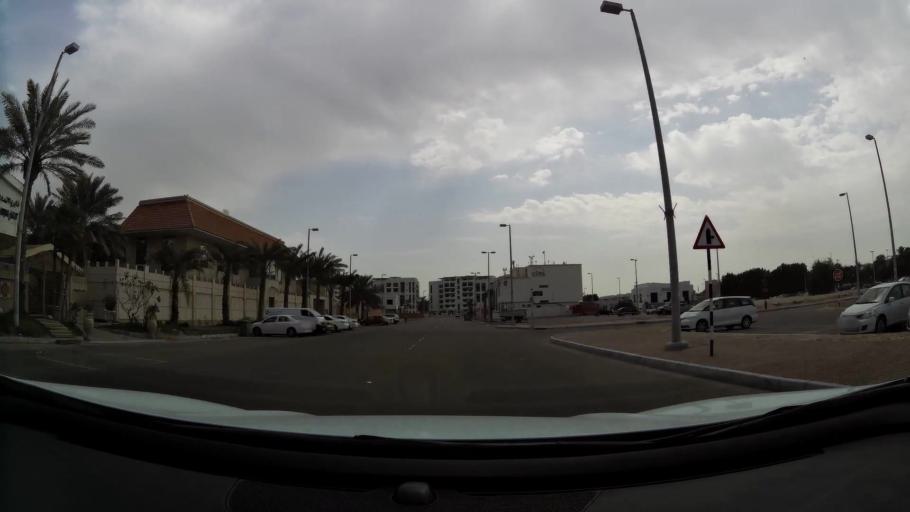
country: AE
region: Abu Dhabi
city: Abu Dhabi
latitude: 24.4603
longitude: 54.3485
